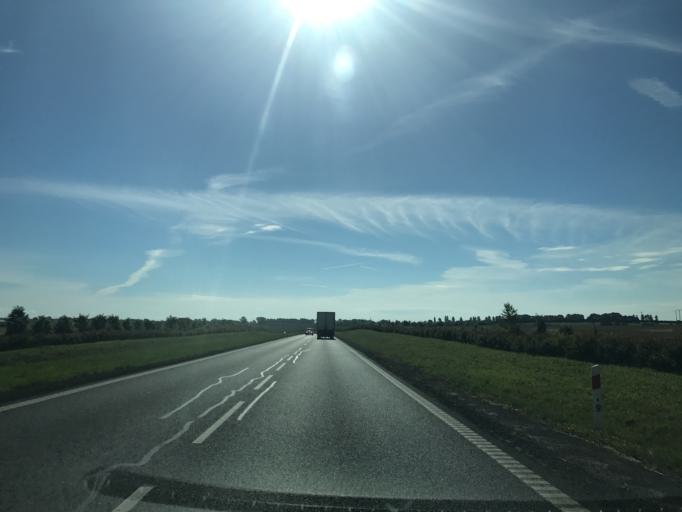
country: PL
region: Pomeranian Voivodeship
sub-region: Powiat chojnicki
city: Chojnice
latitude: 53.6810
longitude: 17.5461
